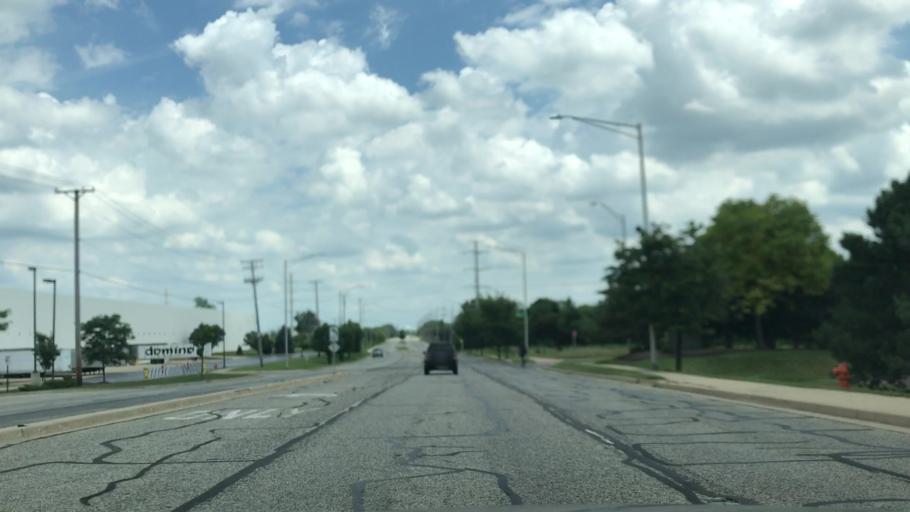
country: US
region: Illinois
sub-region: DuPage County
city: Warrenville
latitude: 41.7989
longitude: -88.2257
